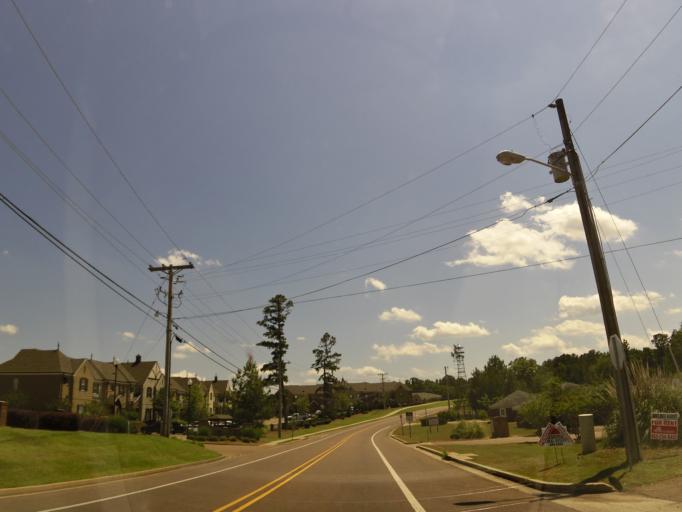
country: US
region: Mississippi
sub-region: Lafayette County
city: University
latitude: 34.3482
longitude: -89.5422
